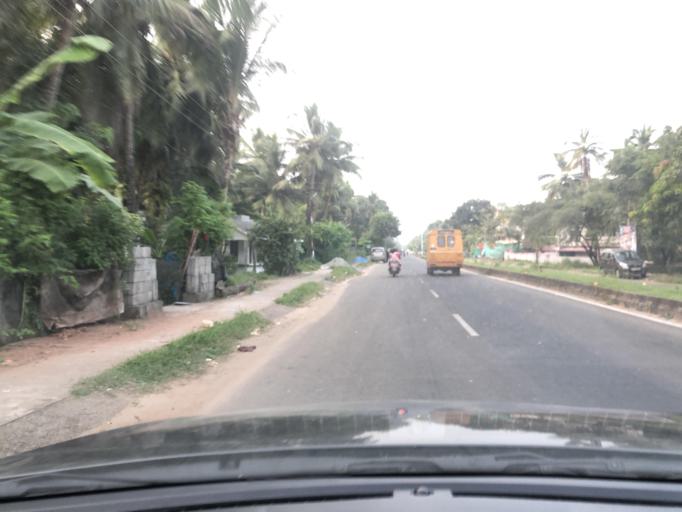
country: IN
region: Kerala
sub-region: Kozhikode
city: Kozhikode
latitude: 11.2934
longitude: 75.7576
